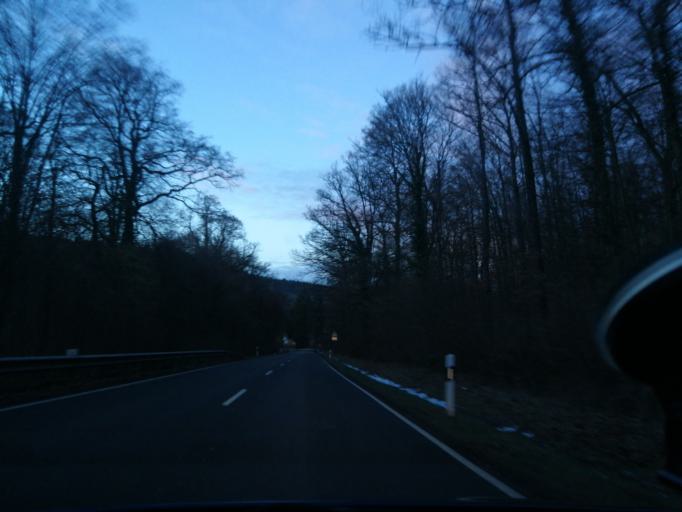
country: DE
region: Rheinland-Pfalz
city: Kenn
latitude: 49.8256
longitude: 6.7099
